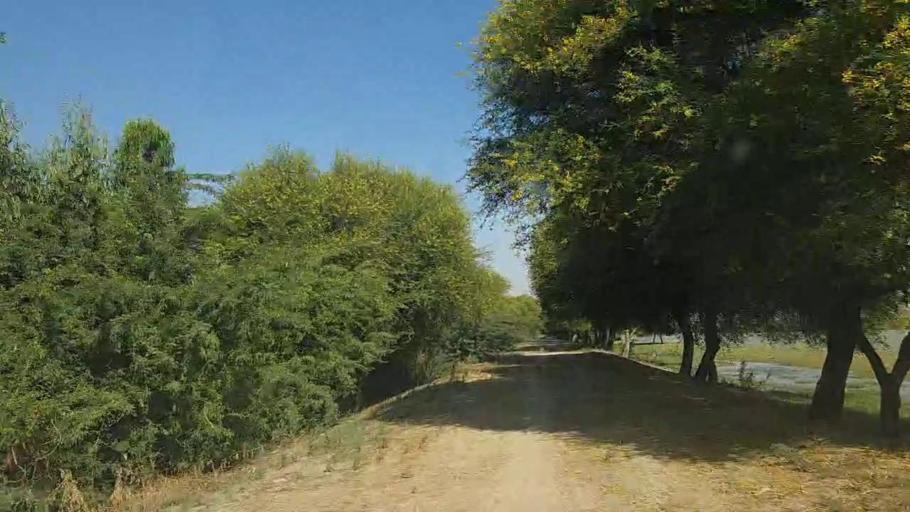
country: PK
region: Sindh
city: Thatta
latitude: 24.7965
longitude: 67.9791
